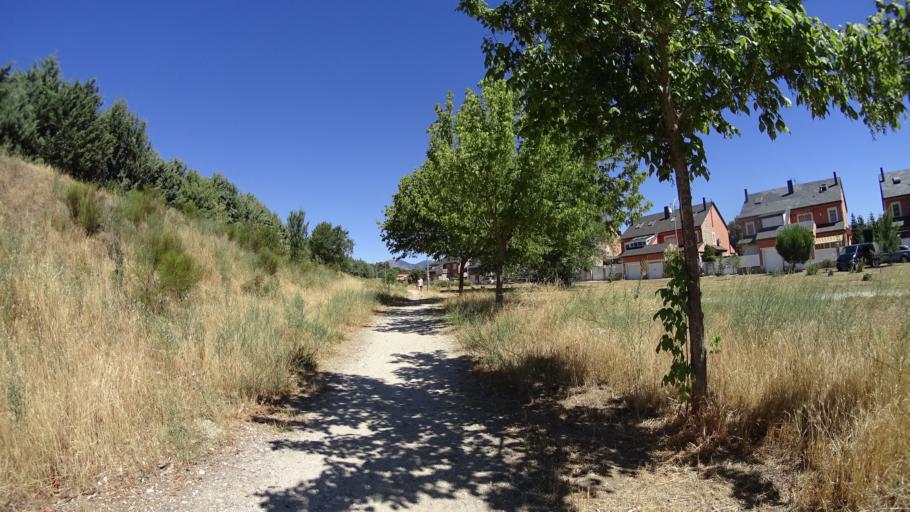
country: ES
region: Madrid
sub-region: Provincia de Madrid
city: Alpedrete
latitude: 40.6452
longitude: -4.0255
